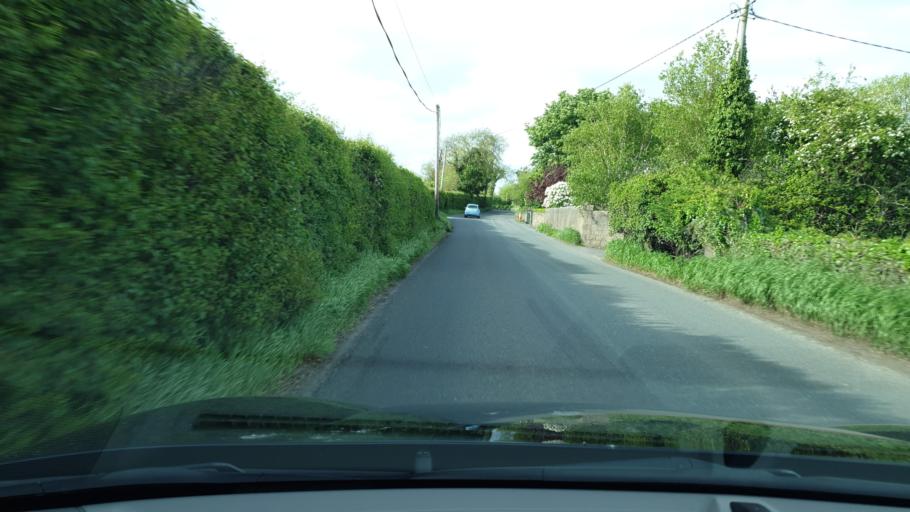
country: IE
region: Leinster
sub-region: An Mhi
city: Ashbourne
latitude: 53.5311
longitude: -6.4072
